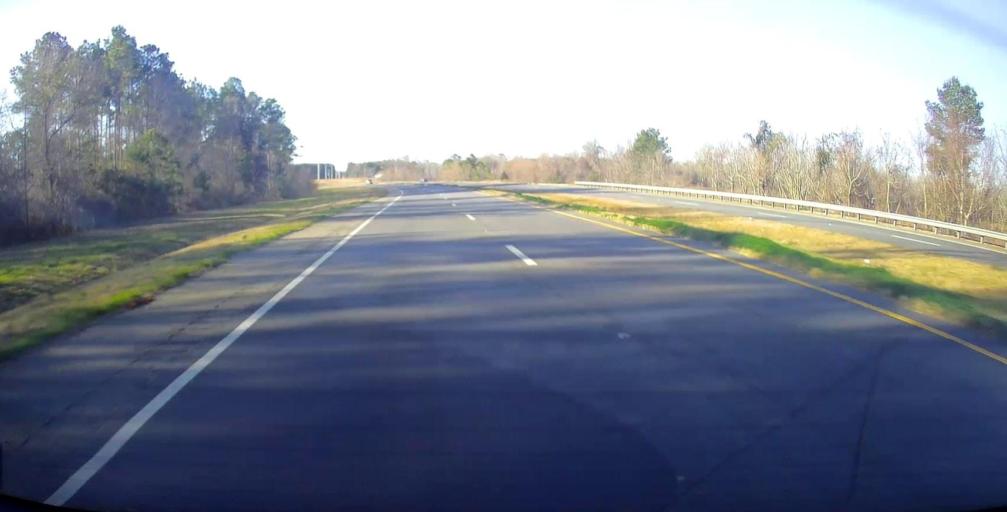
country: US
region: Georgia
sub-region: Lee County
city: Leesburg
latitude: 31.8098
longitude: -84.2090
